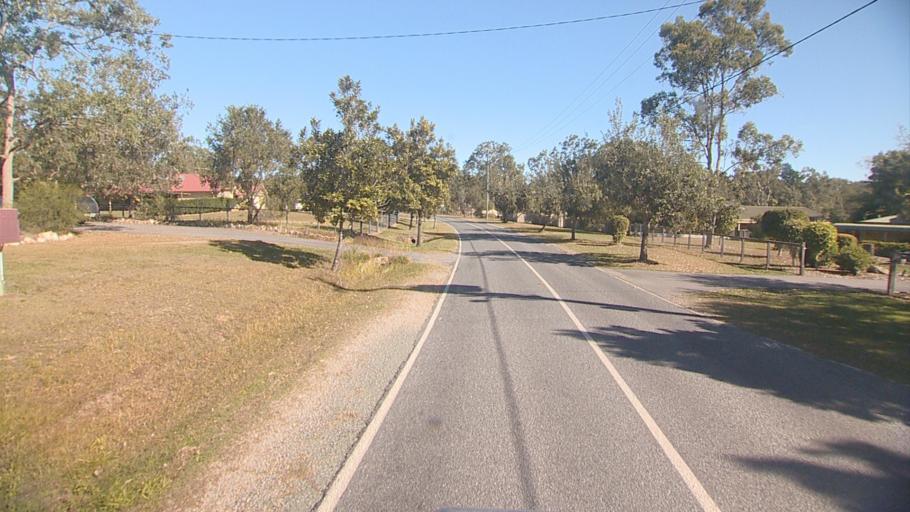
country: AU
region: Queensland
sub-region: Logan
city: North Maclean
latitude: -27.7420
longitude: 152.9564
